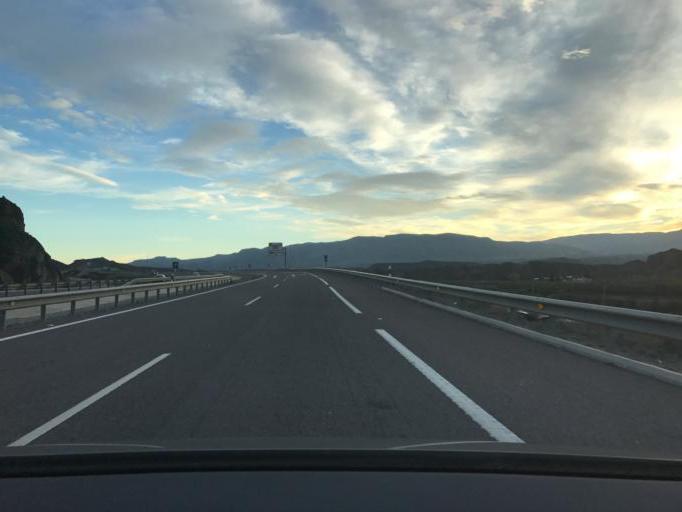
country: ES
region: Andalusia
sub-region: Provincia de Almeria
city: Rioja
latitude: 36.9662
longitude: -2.4659
